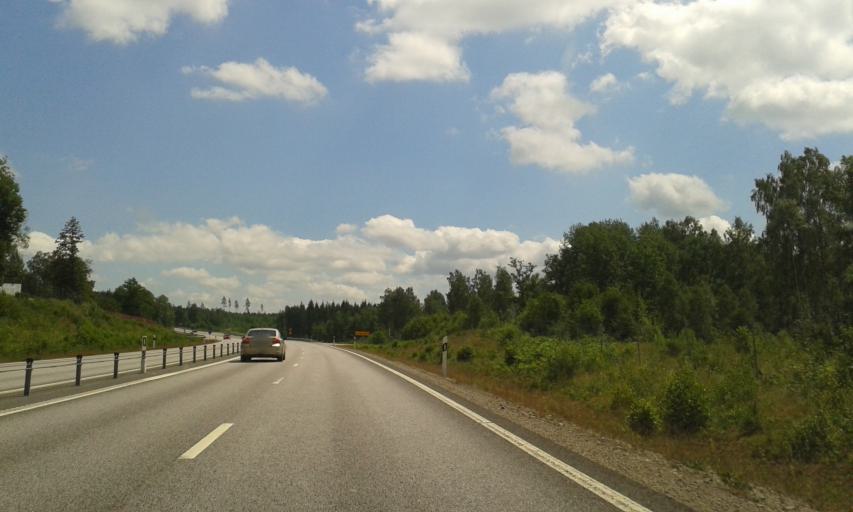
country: SE
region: Kronoberg
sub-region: Vaxjo Kommun
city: Gemla
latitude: 56.8986
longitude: 14.6792
